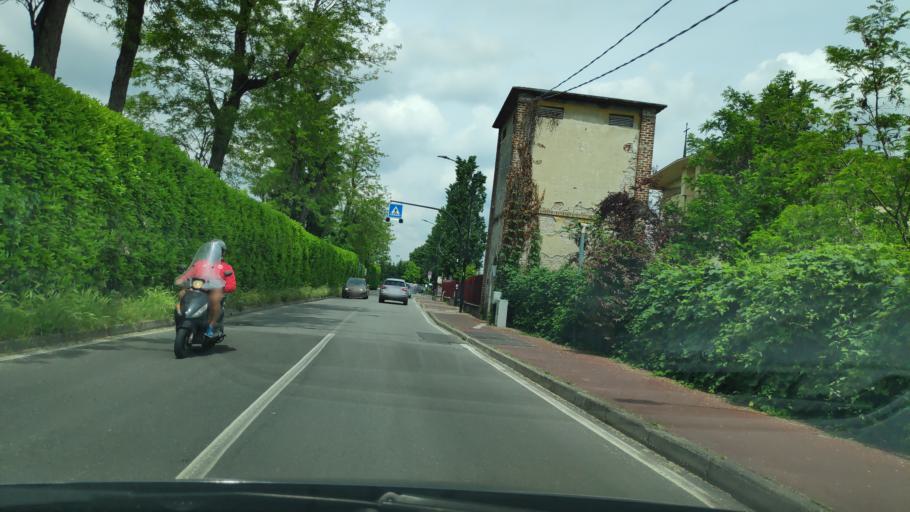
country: IT
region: Lombardy
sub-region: Citta metropolitana di Milano
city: Novegro-Tregarezzo-San Felice
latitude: 45.4715
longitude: 9.2779
